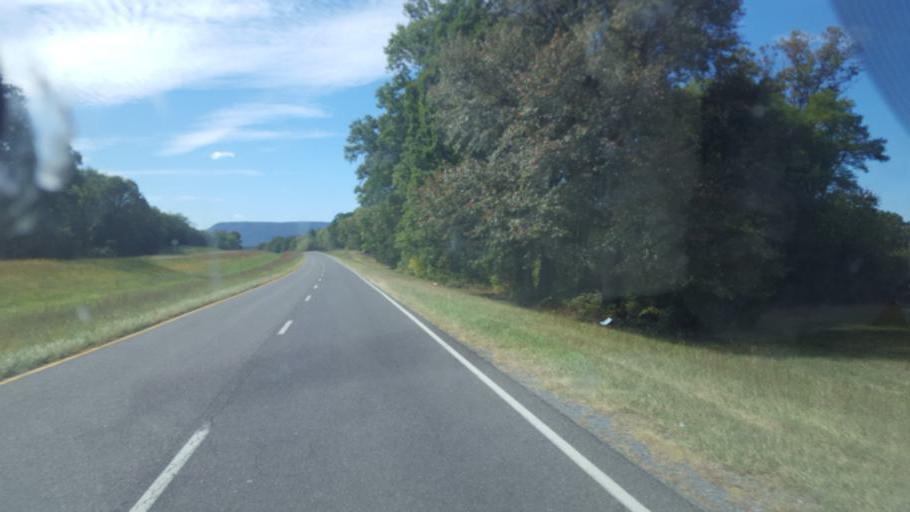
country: US
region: Virginia
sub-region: Page County
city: Luray
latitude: 38.6765
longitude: -78.4263
